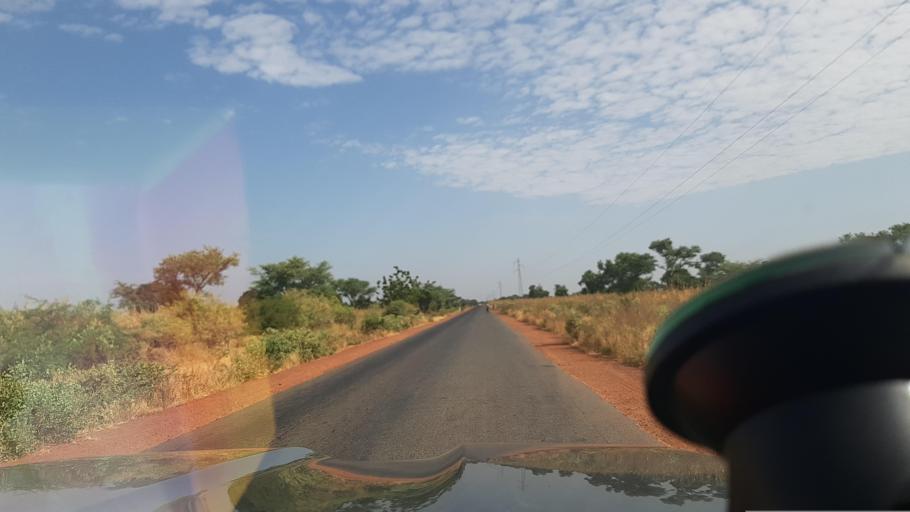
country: ML
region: Segou
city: Markala
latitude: 13.5569
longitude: -6.1137
